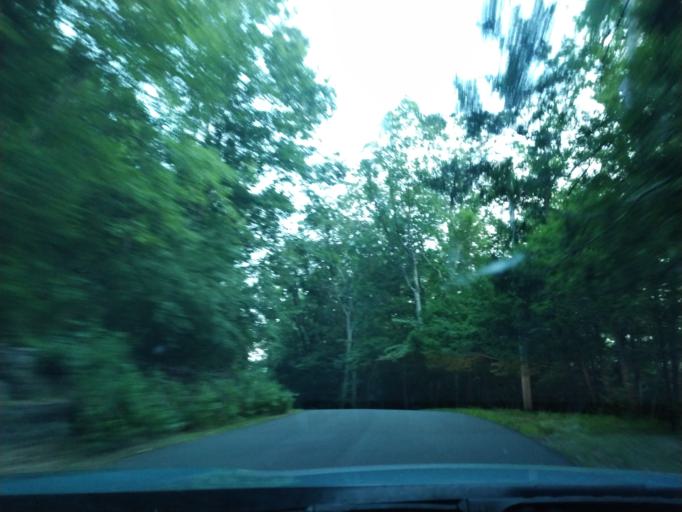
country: US
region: Connecticut
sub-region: New Haven County
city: Southbury
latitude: 41.4242
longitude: -73.2057
